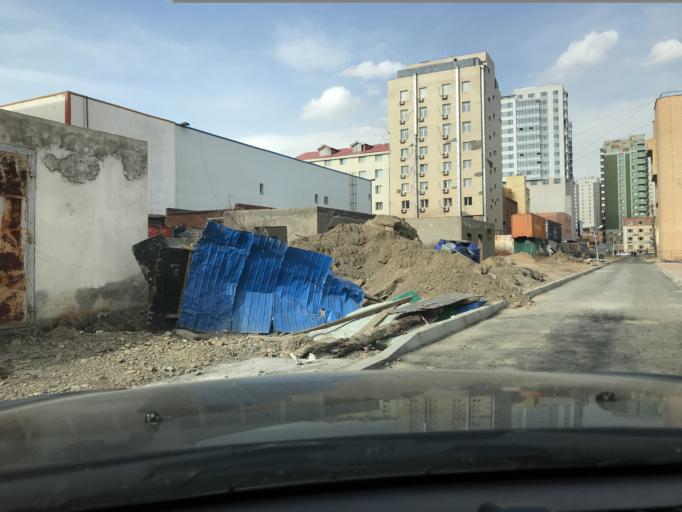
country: MN
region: Ulaanbaatar
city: Ulaanbaatar
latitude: 47.9135
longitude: 106.9450
